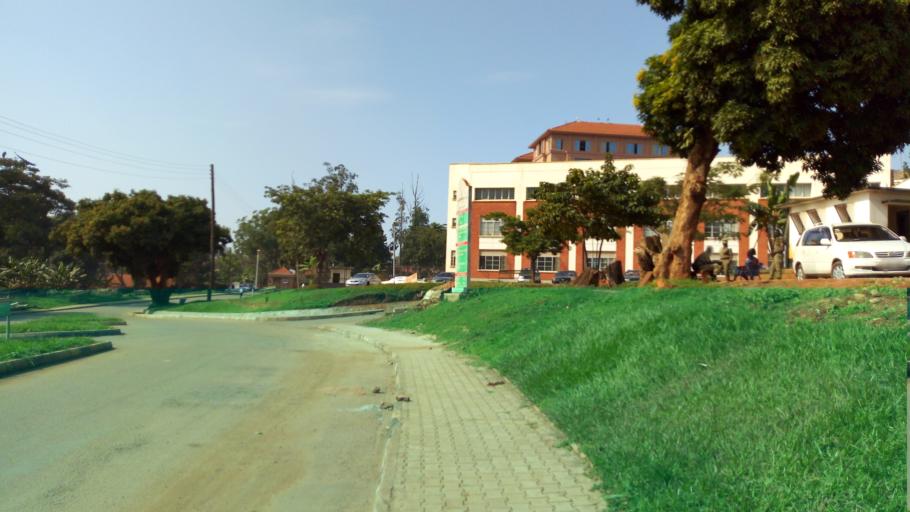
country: UG
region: Central Region
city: Kampala Central Division
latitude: 0.3354
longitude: 32.5711
